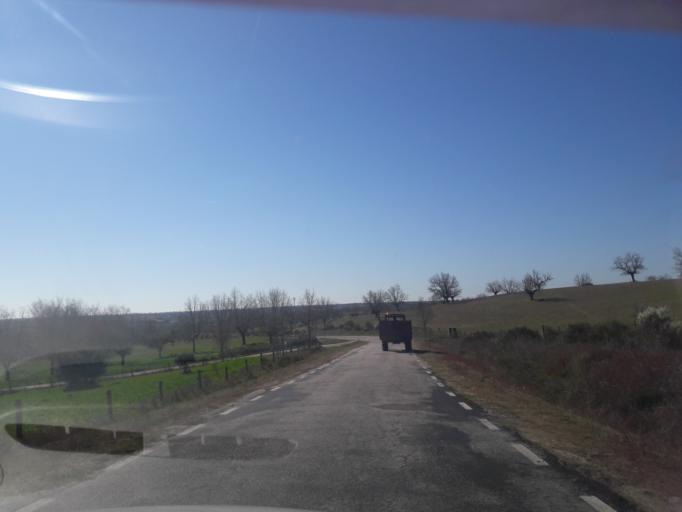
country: ES
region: Castille and Leon
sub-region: Provincia de Salamanca
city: Valsalabroso
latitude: 41.1658
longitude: -6.5000
